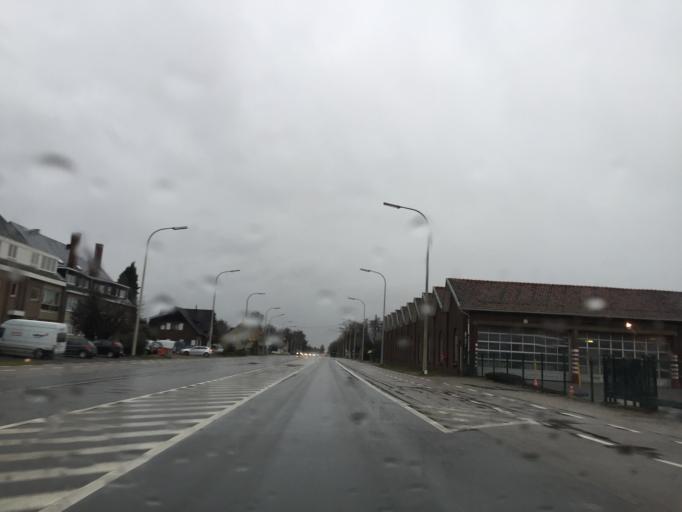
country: BE
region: Flanders
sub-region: Provincie Limburg
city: Lanaken
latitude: 50.8998
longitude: 5.6774
